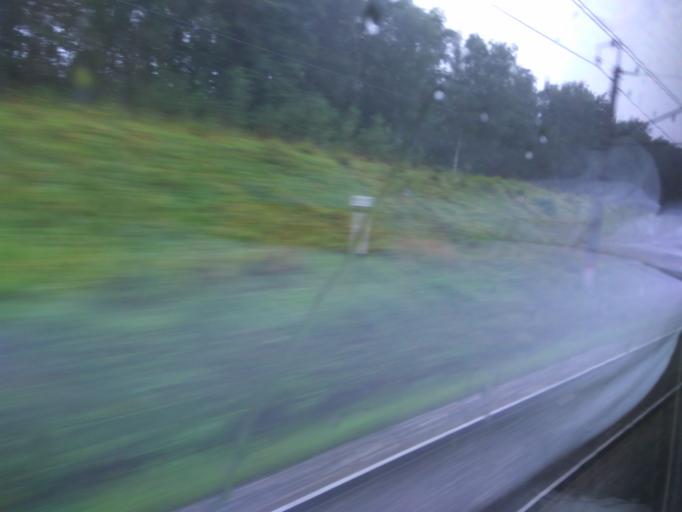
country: RU
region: Moskovskaya
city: Ozherel'ye
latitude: 54.8259
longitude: 38.2525
